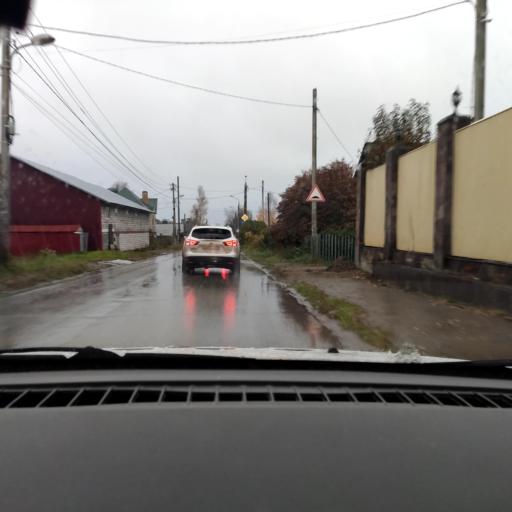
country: RU
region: Perm
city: Kondratovo
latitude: 58.0459
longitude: 56.1197
